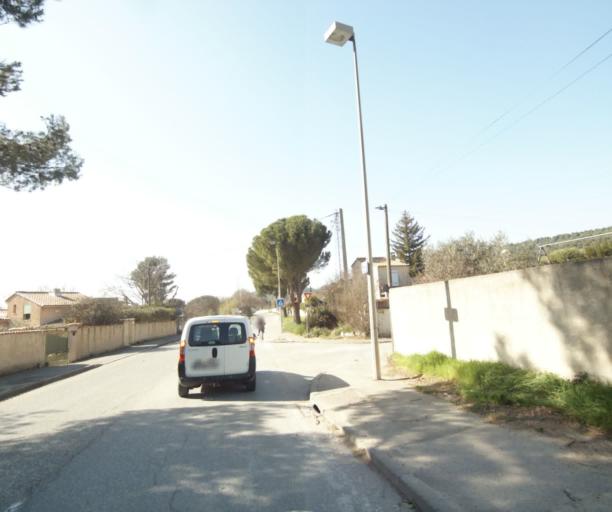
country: FR
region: Provence-Alpes-Cote d'Azur
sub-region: Departement des Bouches-du-Rhone
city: Bouc-Bel-Air
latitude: 43.4477
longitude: 5.4284
